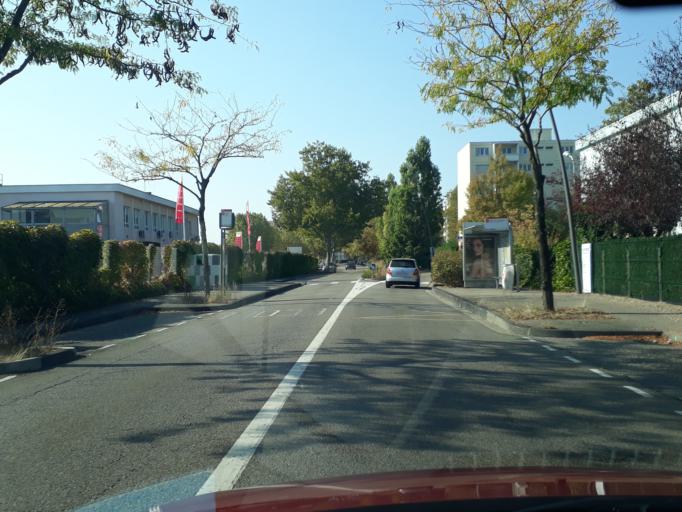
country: FR
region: Rhone-Alpes
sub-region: Departement du Rhone
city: Saint-Priest
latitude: 45.6854
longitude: 4.9429
